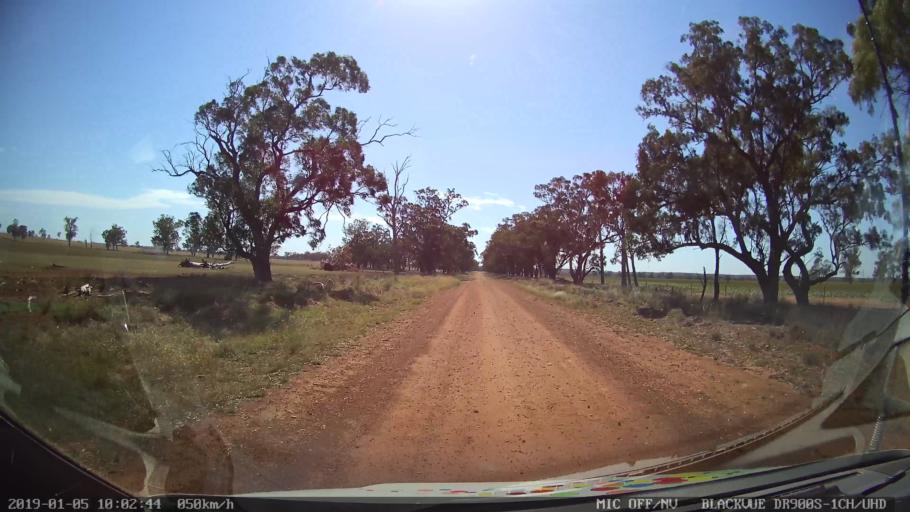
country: AU
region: New South Wales
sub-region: Gilgandra
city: Gilgandra
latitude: -31.6711
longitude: 148.8459
